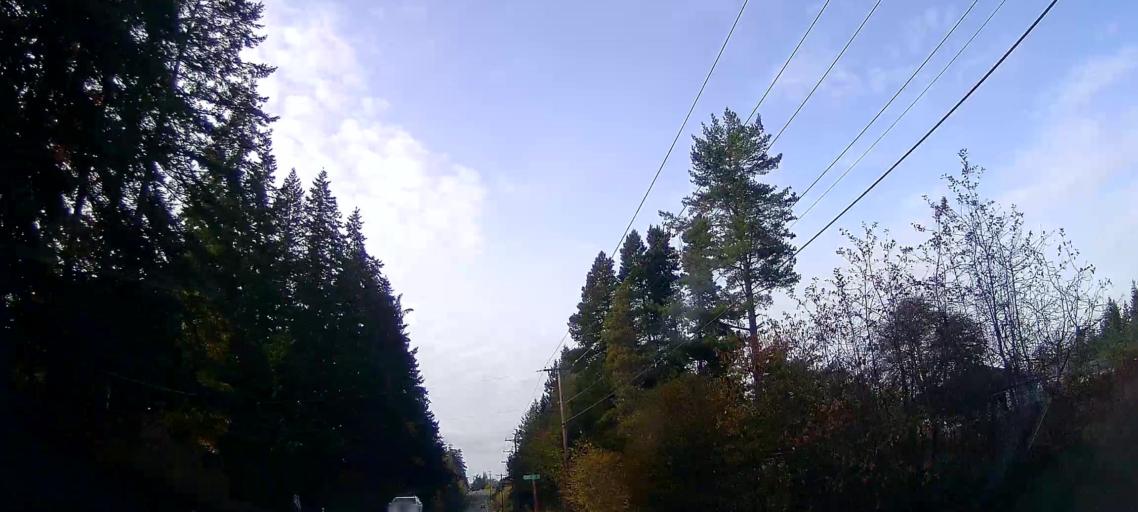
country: US
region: Washington
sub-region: Snohomish County
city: Stanwood
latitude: 48.2501
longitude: -122.4637
